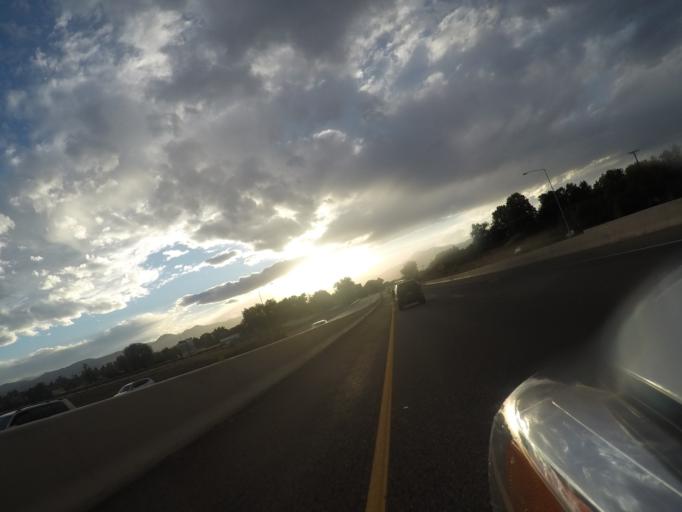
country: US
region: Colorado
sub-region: Jefferson County
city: Lakewood
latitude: 39.6529
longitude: -105.0837
